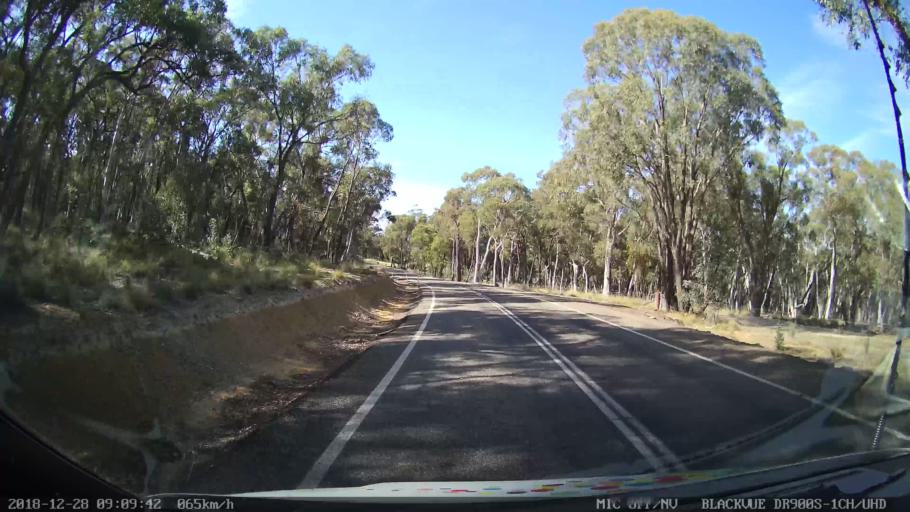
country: AU
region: New South Wales
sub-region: Upper Lachlan Shire
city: Crookwell
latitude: -34.2240
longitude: 149.3360
